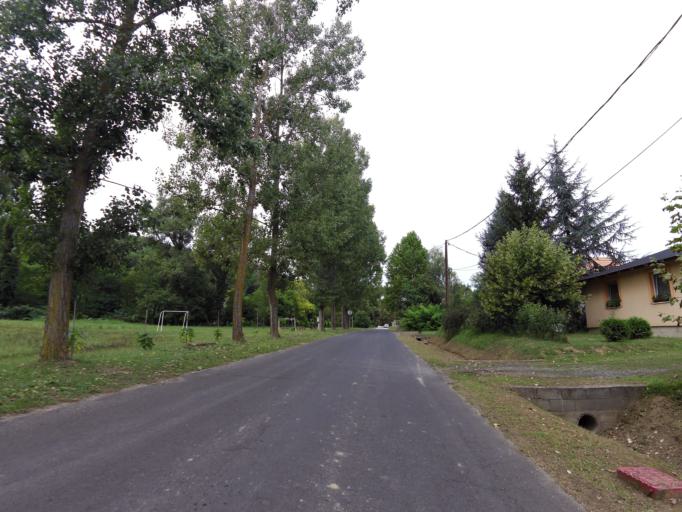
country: HU
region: Zala
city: Vonyarcvashegy
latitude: 46.8432
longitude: 17.3505
